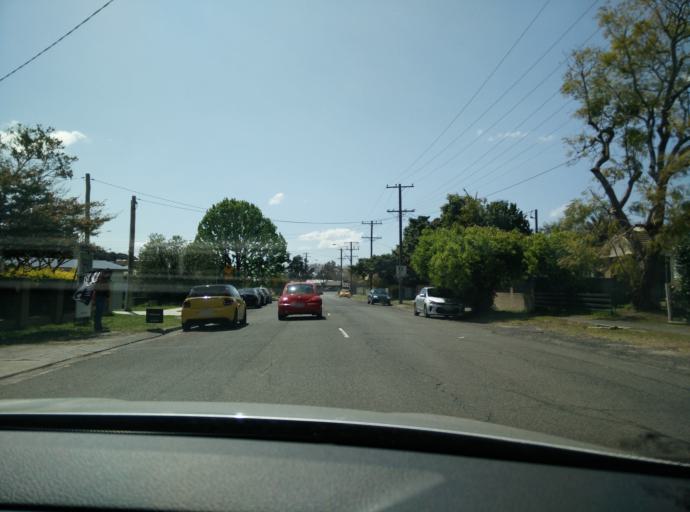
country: AU
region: New South Wales
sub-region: Gosford Shire
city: Blackwall
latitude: -33.4934
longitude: 151.3115
